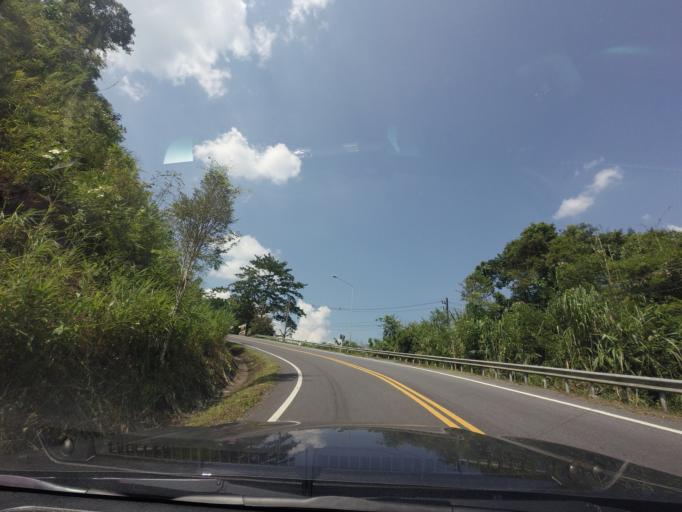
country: TH
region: Nan
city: Bo Kluea
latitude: 19.0813
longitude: 101.1490
